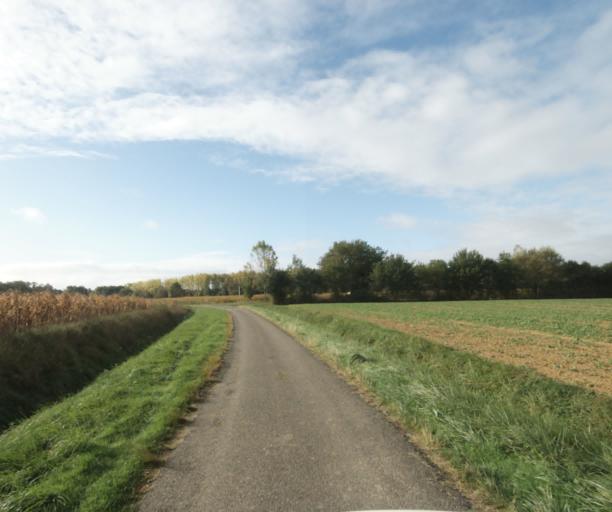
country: FR
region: Midi-Pyrenees
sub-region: Departement du Gers
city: Nogaro
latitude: 43.8069
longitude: -0.0670
